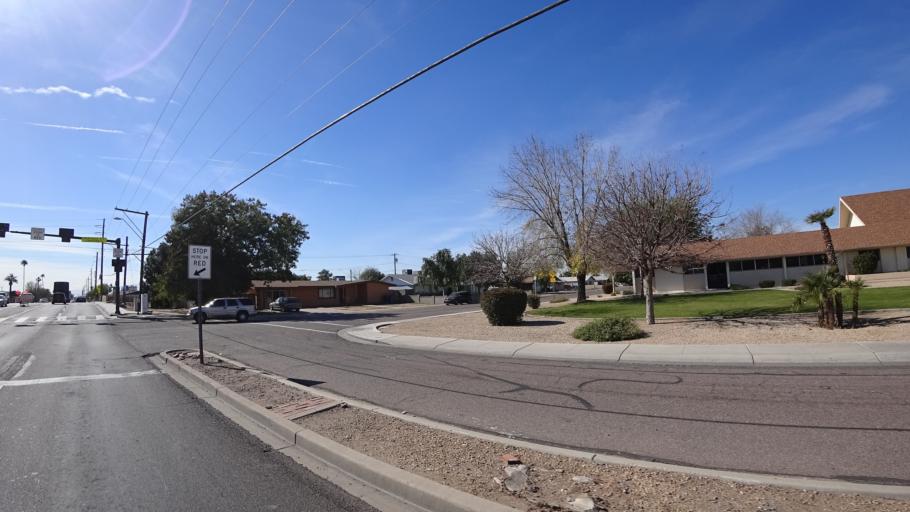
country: US
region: Arizona
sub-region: Maricopa County
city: Glendale
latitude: 33.4919
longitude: -112.1866
